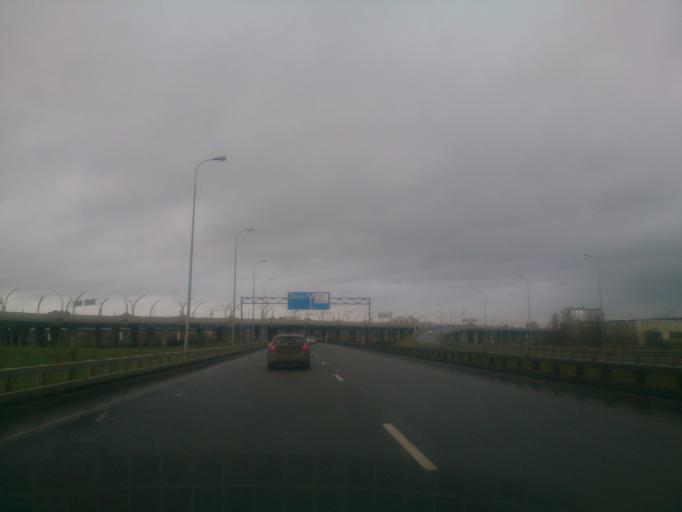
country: RU
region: St.-Petersburg
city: Dachnoye
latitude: 59.8341
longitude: 30.2833
